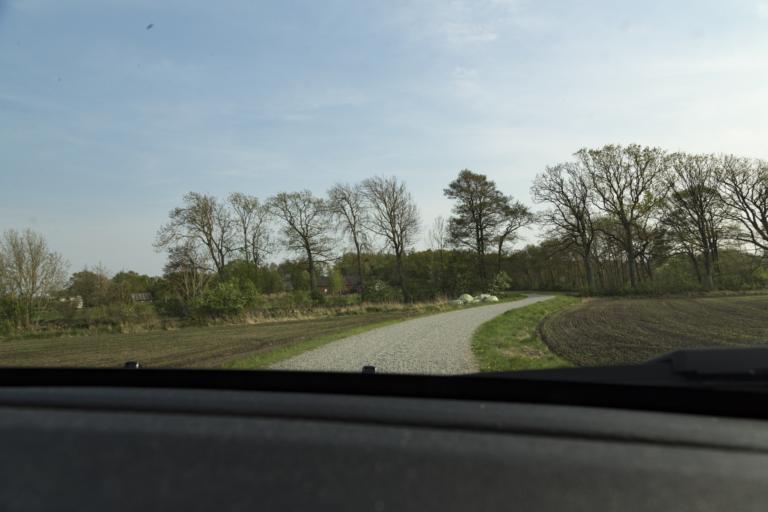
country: SE
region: Halland
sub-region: Varbergs Kommun
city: Varberg
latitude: 57.1570
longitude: 12.2618
